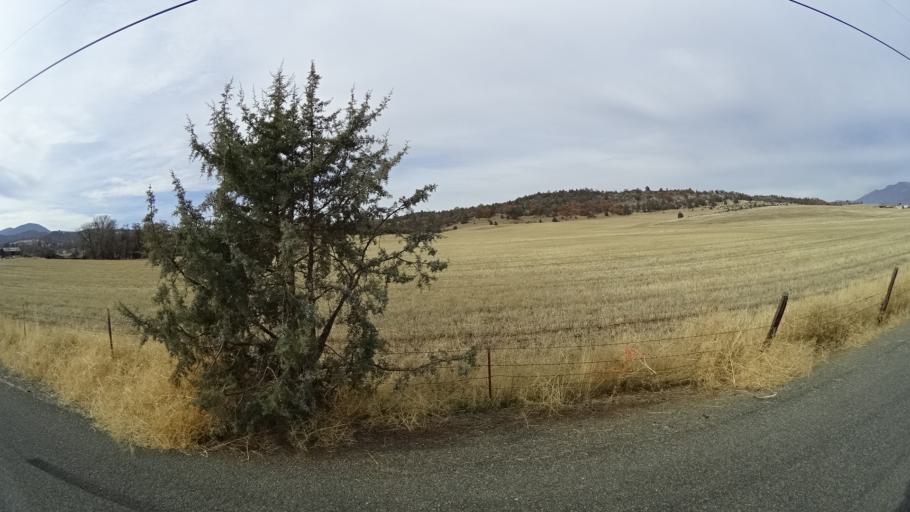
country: US
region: California
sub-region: Siskiyou County
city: Montague
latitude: 41.6957
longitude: -122.5639
